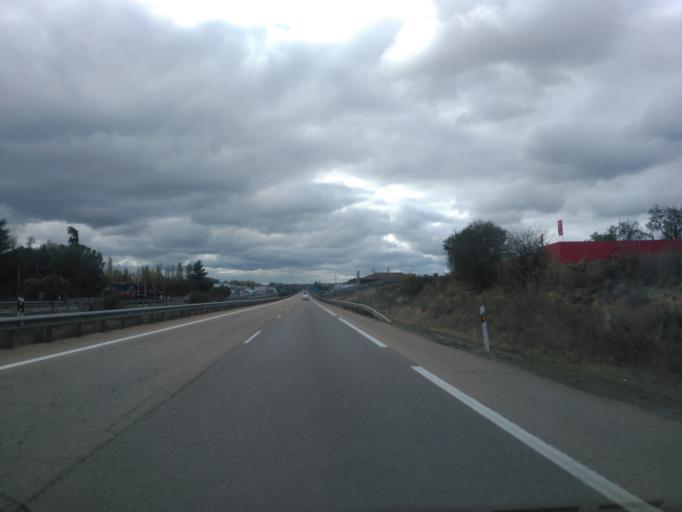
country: ES
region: Castille and Leon
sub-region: Provincia de Valladolid
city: Santovenia de Pisuerga
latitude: 41.7214
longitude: -4.6925
